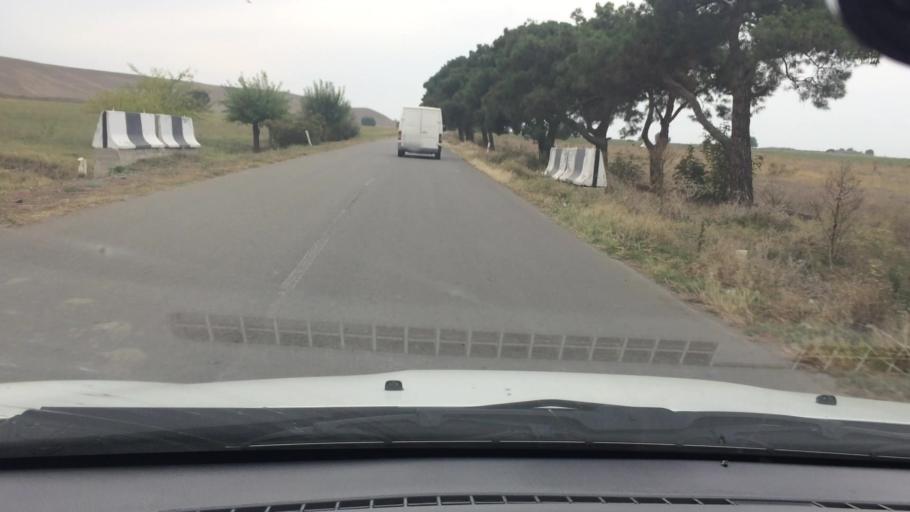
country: AM
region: Tavush
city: Berdavan
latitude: 41.3351
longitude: 45.0281
